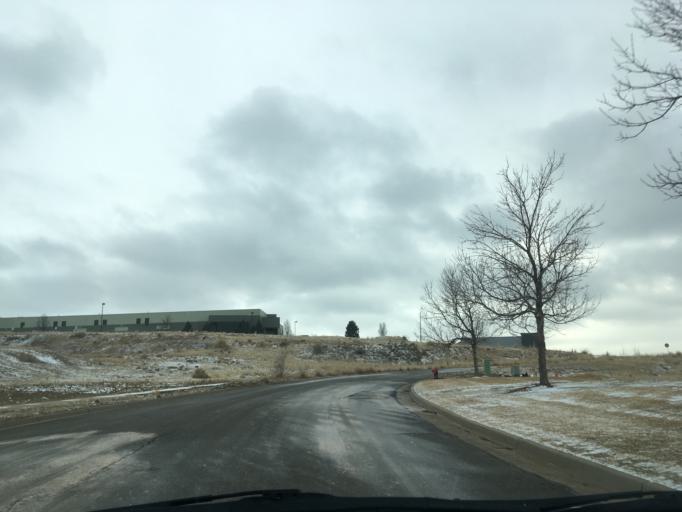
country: US
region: Colorado
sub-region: Boulder County
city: Lafayette
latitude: 39.9780
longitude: -105.0669
